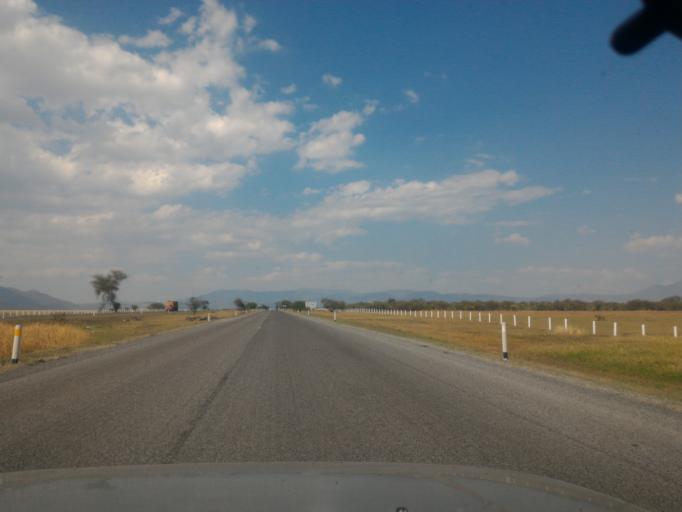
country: MX
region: Jalisco
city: Atoyac
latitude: 20.0261
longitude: -103.5298
